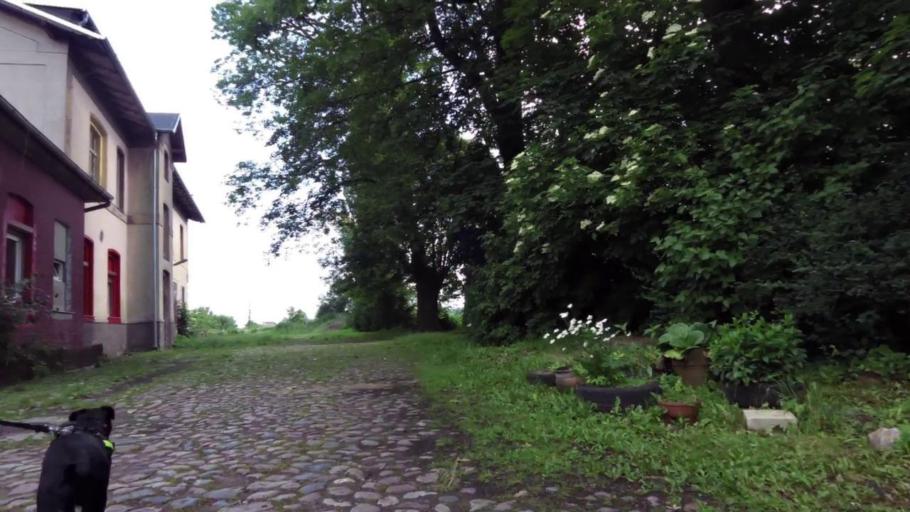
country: PL
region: West Pomeranian Voivodeship
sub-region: Powiat pyrzycki
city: Lipiany
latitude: 52.9565
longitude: 14.9557
